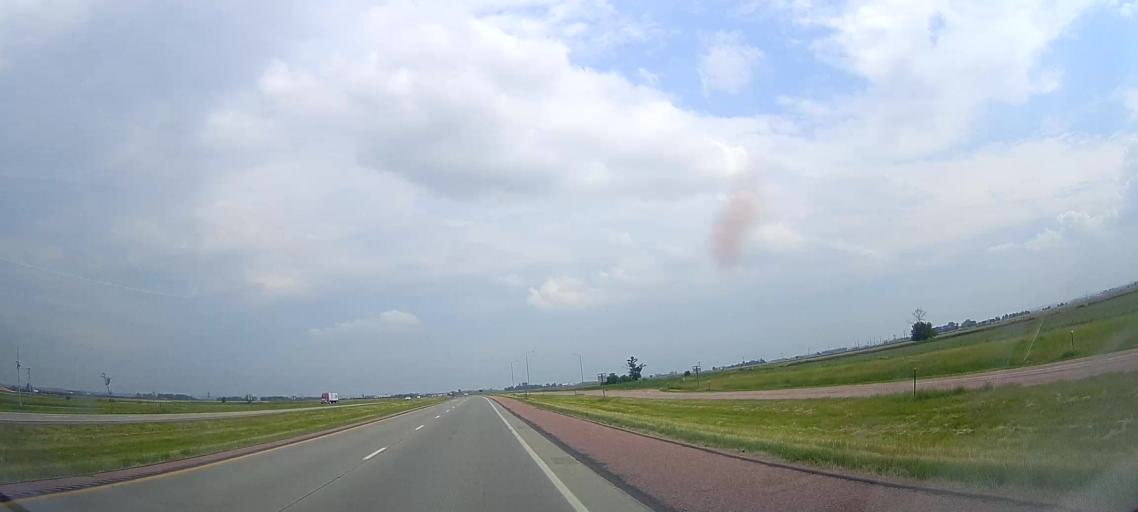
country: US
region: South Dakota
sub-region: Union County
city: Elk Point
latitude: 42.6432
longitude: -96.6277
